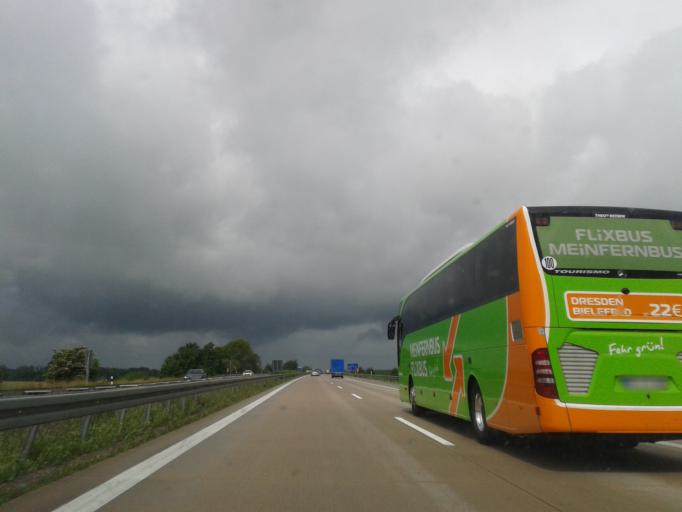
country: DE
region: Saxony
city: Mutzschen
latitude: 51.2442
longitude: 12.8550
